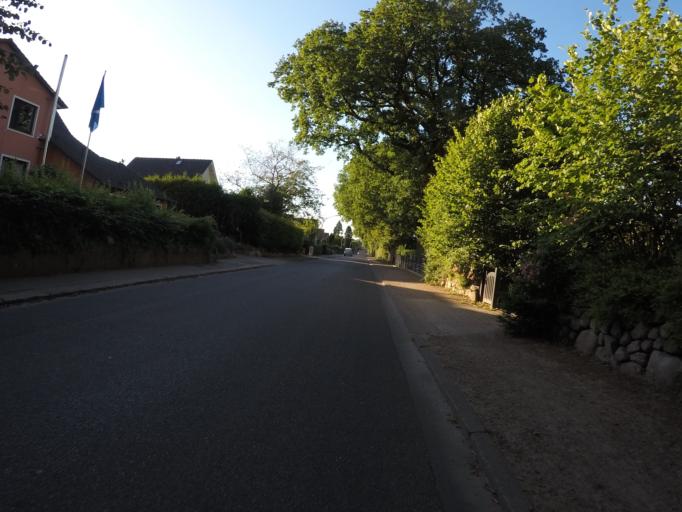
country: DE
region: Hamburg
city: Duvenstedt
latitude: 53.7028
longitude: 10.1112
